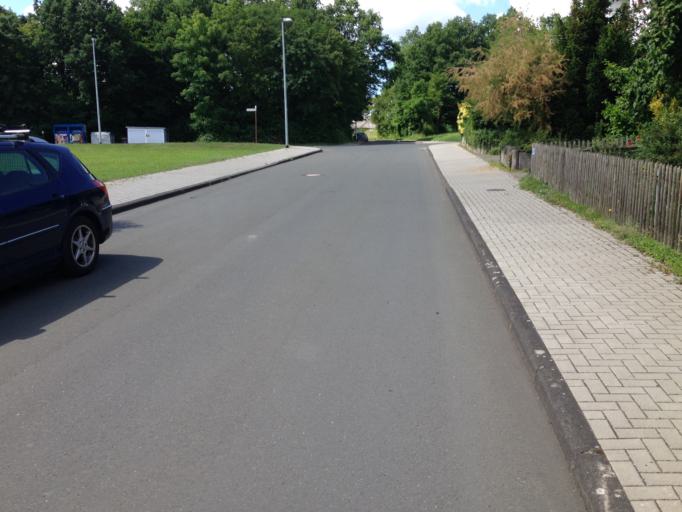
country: DE
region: Hesse
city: Allendorf an der Lahn
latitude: 50.5537
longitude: 8.6253
